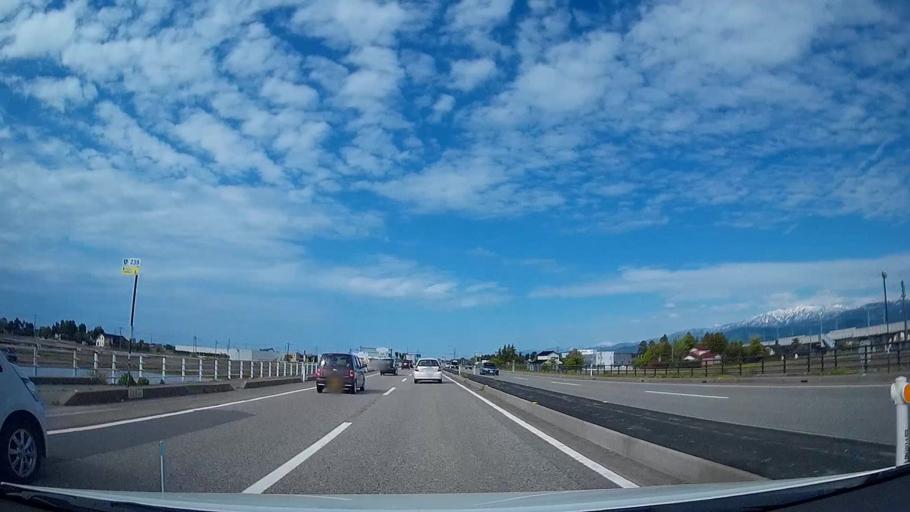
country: JP
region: Toyama
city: Namerikawa
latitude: 36.7354
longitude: 137.3369
